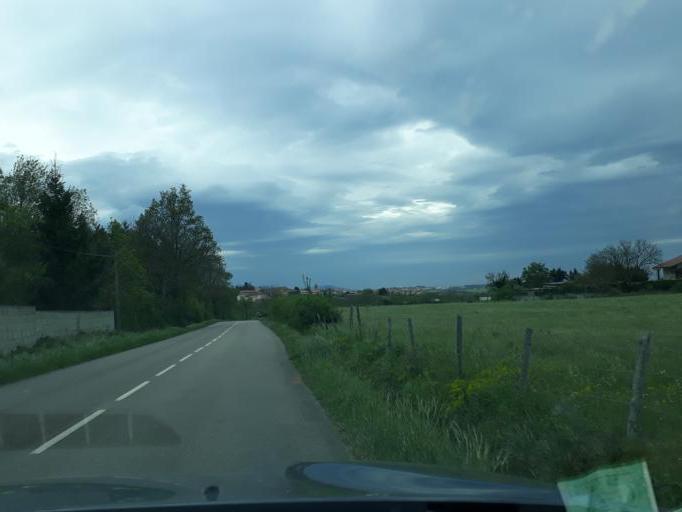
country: FR
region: Rhone-Alpes
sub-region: Departement du Rhone
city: Soucieu-en-Jarrest
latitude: 45.6674
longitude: 4.6958
